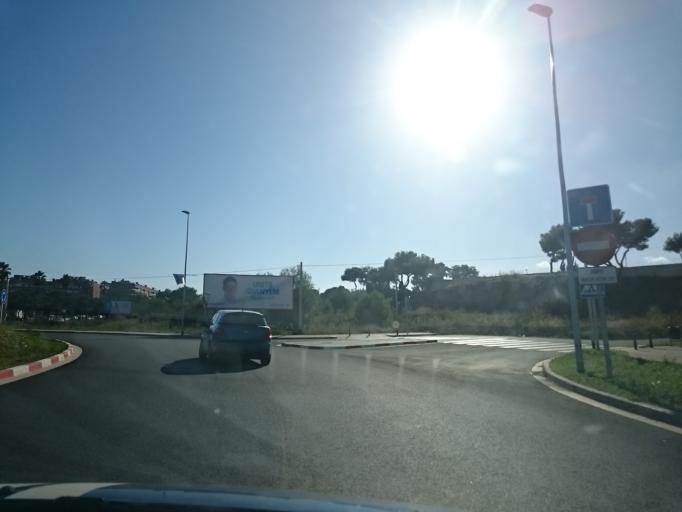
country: ES
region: Catalonia
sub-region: Provincia de Barcelona
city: Viladecans
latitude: 41.3230
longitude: 2.0291
